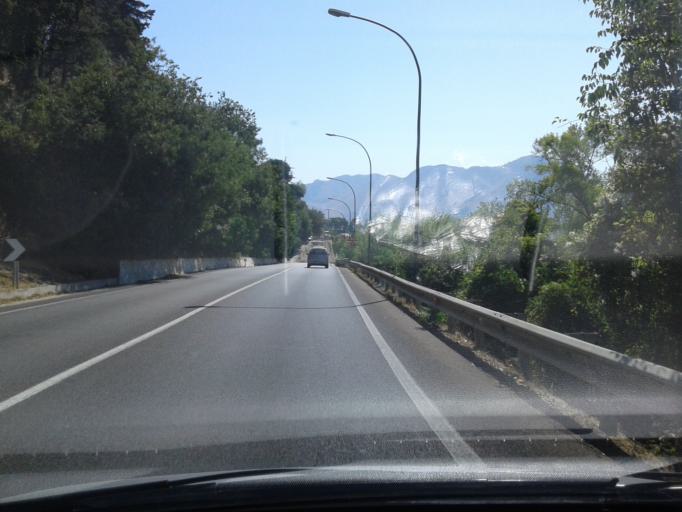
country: IT
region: Sicily
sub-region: Palermo
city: Cannizzaro-Favara
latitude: 38.0718
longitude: 13.2729
